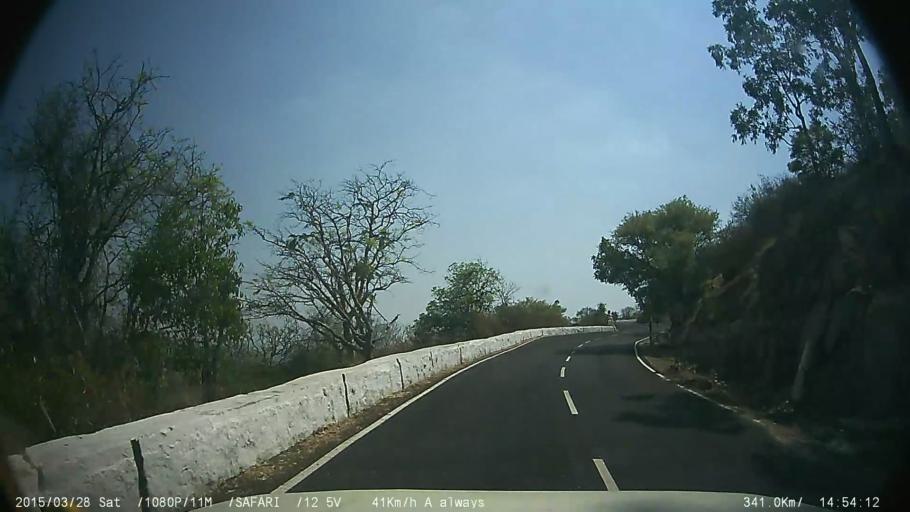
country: IN
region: Karnataka
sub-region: Mysore
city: Mysore
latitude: 12.2837
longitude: 76.6959
